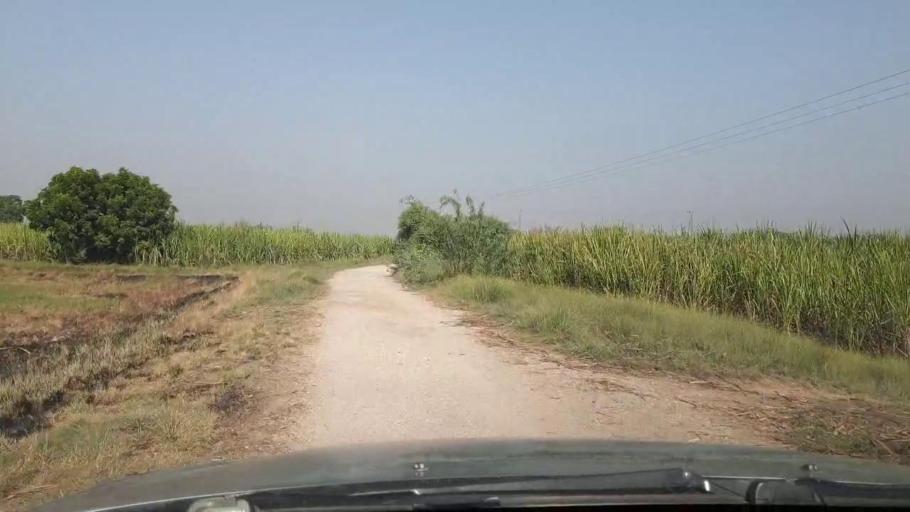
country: PK
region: Sindh
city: Tando Jam
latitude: 25.2826
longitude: 68.5342
